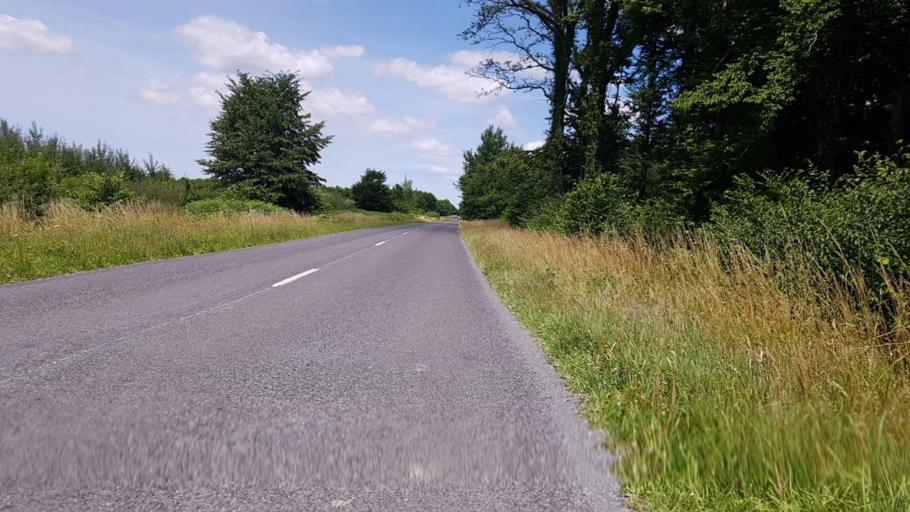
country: FR
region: Picardie
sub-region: Departement de l'Oise
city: Carlepont
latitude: 49.5226
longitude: 2.9835
